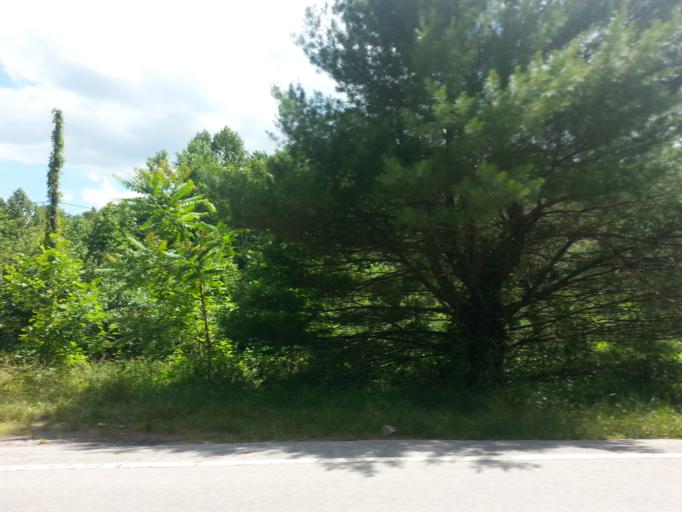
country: US
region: Virginia
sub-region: Lee County
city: Jonesville
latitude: 36.7618
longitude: -83.1271
